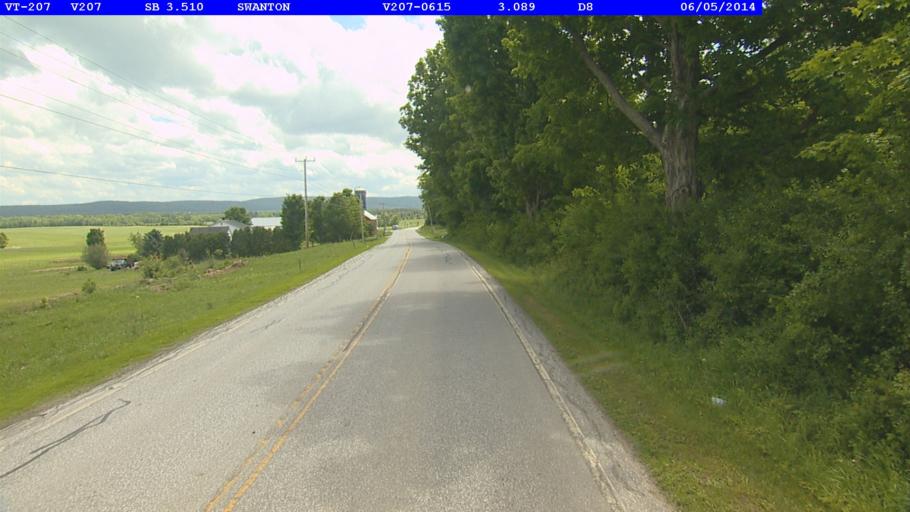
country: US
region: Vermont
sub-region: Franklin County
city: Swanton
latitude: 44.8886
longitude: -73.0678
